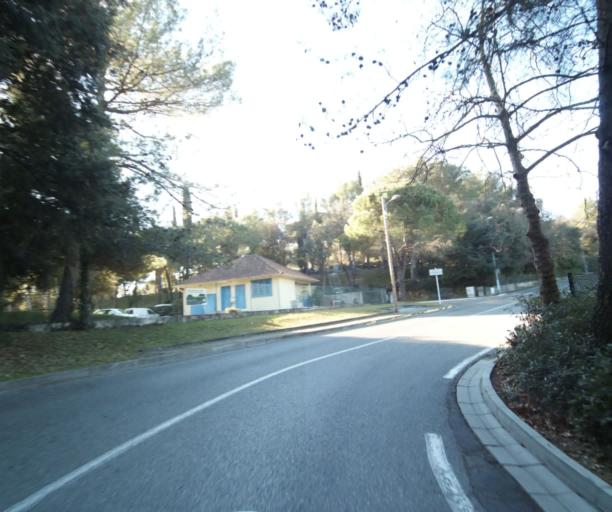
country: FR
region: Provence-Alpes-Cote d'Azur
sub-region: Departement des Alpes-Maritimes
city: Vallauris
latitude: 43.6009
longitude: 7.0731
